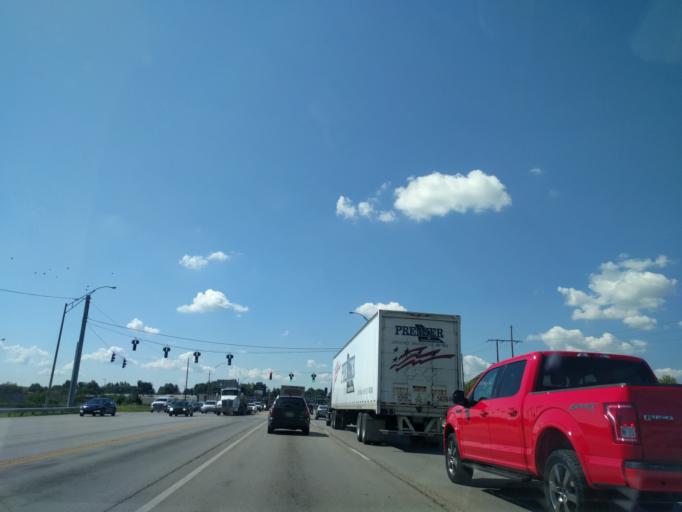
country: US
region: Kentucky
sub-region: Fayette County
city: Monticello
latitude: 37.9955
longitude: -84.5221
